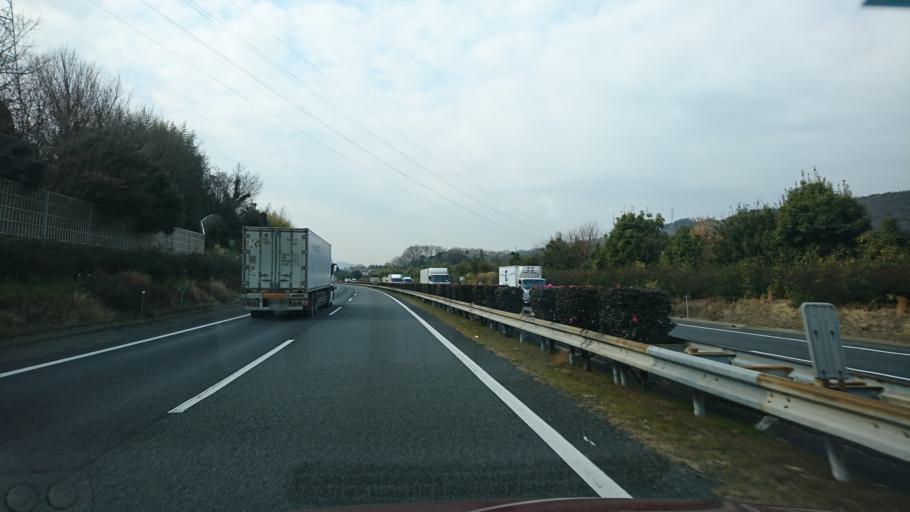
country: JP
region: Hiroshima
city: Kannabecho-yahiro
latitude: 34.5217
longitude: 133.4267
